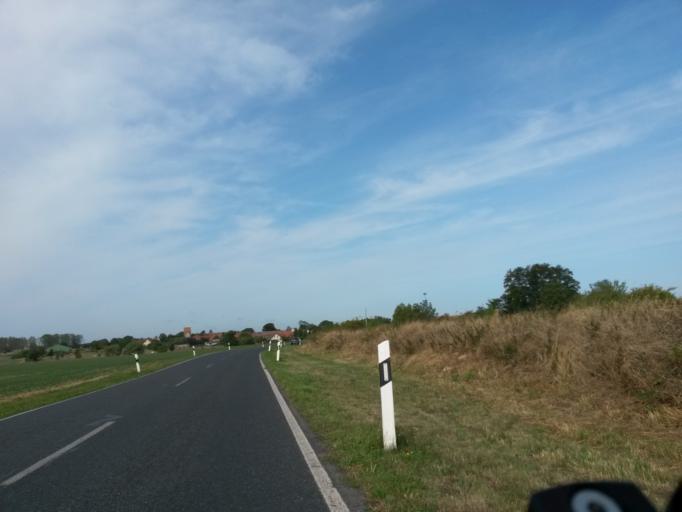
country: DE
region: Saxony-Anhalt
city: Tangermunde
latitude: 52.5406
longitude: 11.9021
